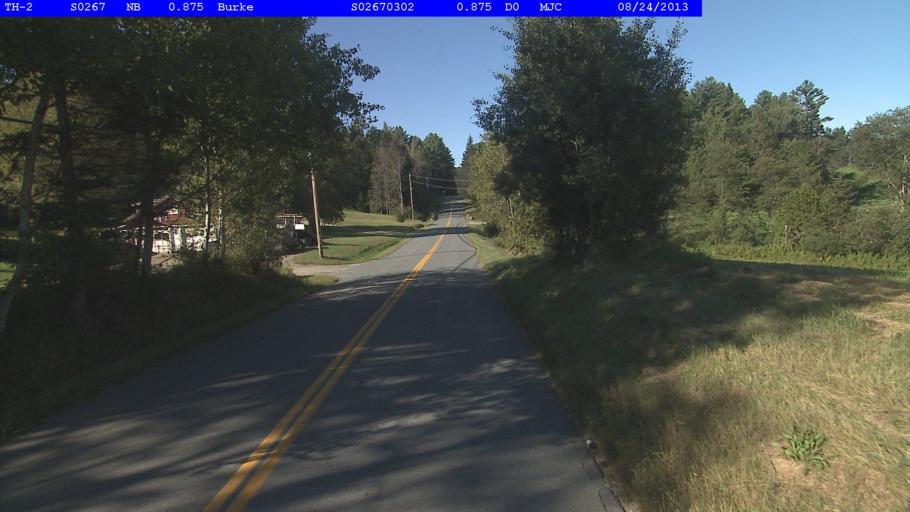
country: US
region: Vermont
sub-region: Caledonia County
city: Lyndonville
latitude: 44.5992
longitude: -71.9414
